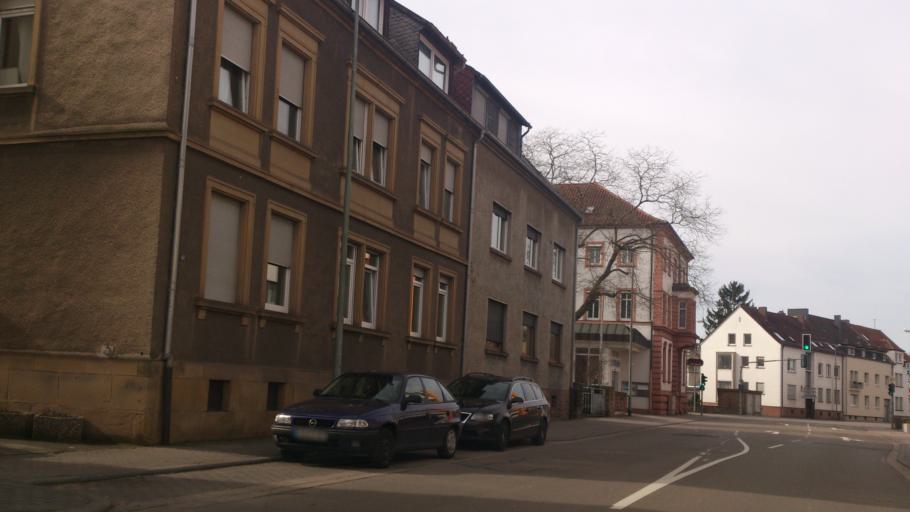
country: DE
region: Rheinland-Pfalz
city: Zweibrucken
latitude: 49.2477
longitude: 7.3599
